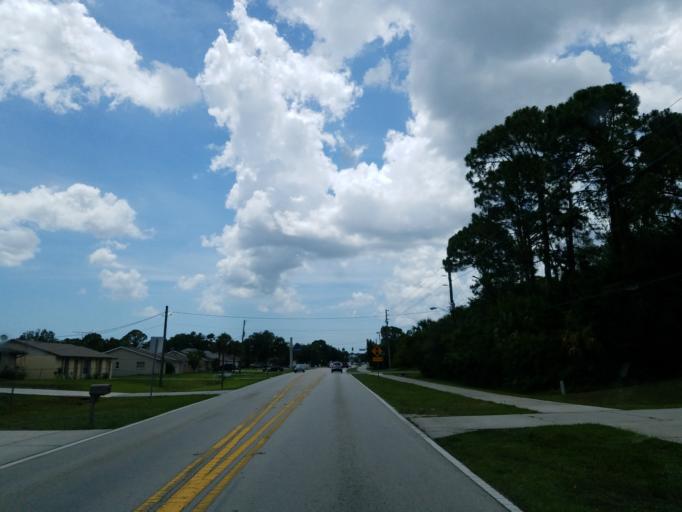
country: US
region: Florida
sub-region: Sarasota County
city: North Port
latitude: 27.0689
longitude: -82.1955
